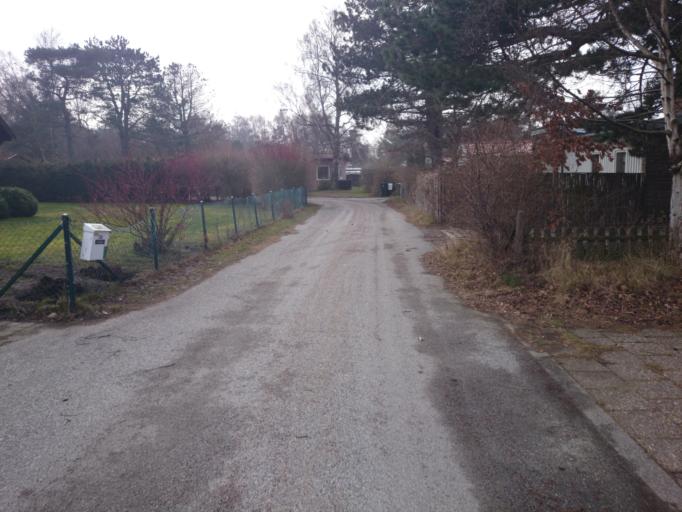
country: SE
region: Skane
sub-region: Vellinge Kommun
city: Skanor med Falsterbo
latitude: 55.3948
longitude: 12.8532
